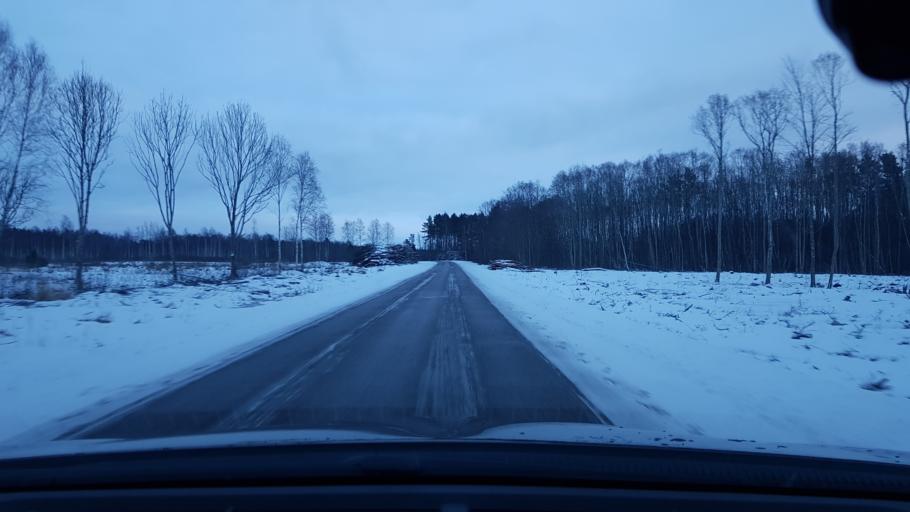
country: EE
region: Laeaene
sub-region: Haapsalu linn
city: Haapsalu
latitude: 59.0734
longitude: 23.5695
